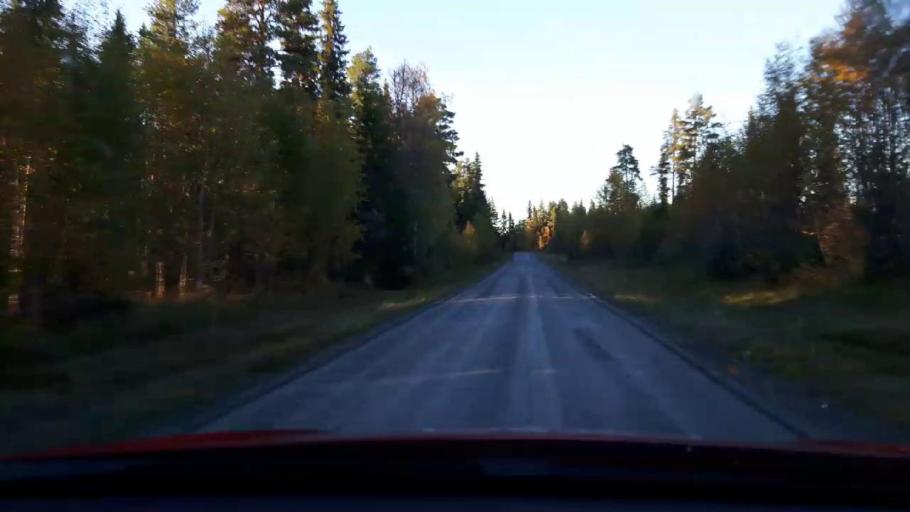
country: SE
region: Jaemtland
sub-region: Krokoms Kommun
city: Krokom
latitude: 63.4419
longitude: 14.4218
